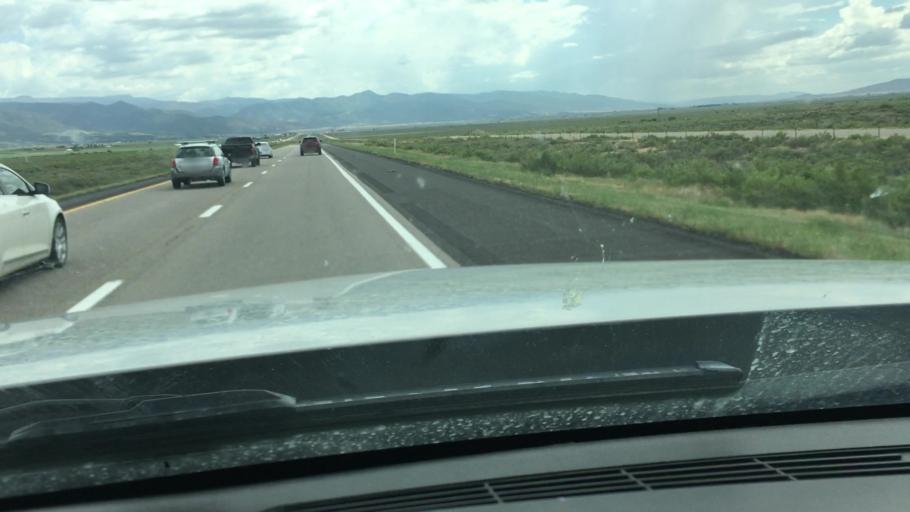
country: US
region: Utah
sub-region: Iron County
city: Parowan
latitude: 37.9556
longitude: -112.7519
